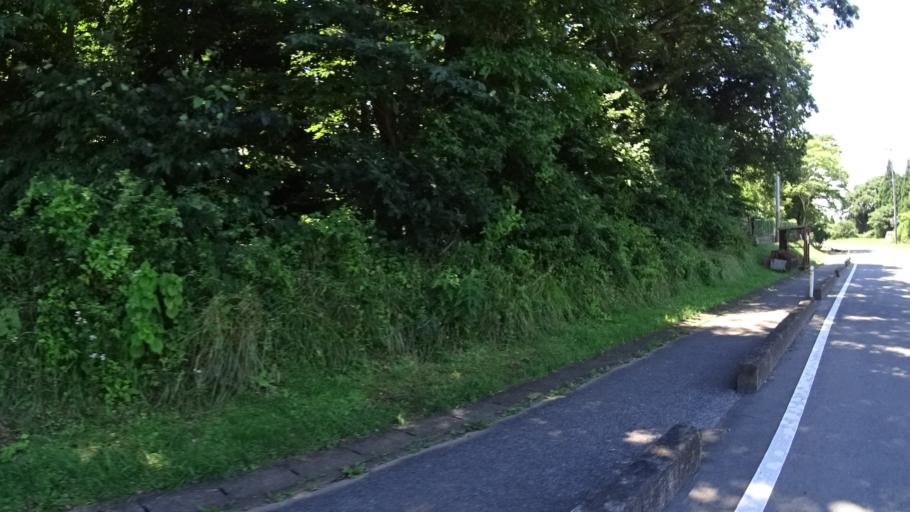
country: JP
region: Iwate
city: Ofunato
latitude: 38.8408
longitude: 141.6252
